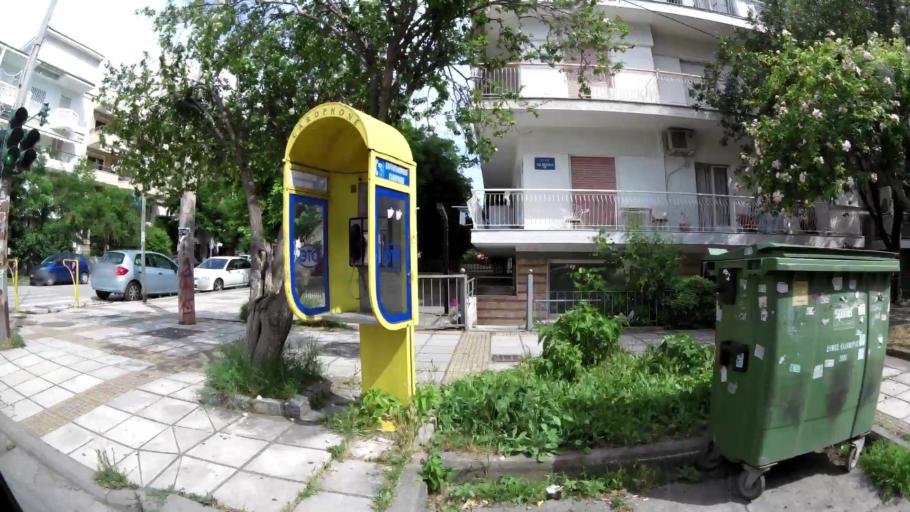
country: GR
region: Central Macedonia
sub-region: Nomos Thessalonikis
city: Kalamaria
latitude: 40.5902
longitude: 22.9484
